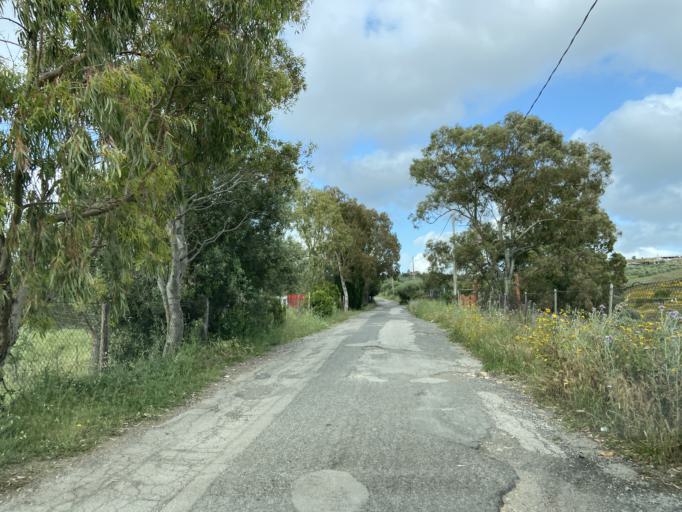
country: IT
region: Latium
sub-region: Citta metropolitana di Roma Capitale
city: Santa Marinella
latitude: 42.0805
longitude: 11.8426
